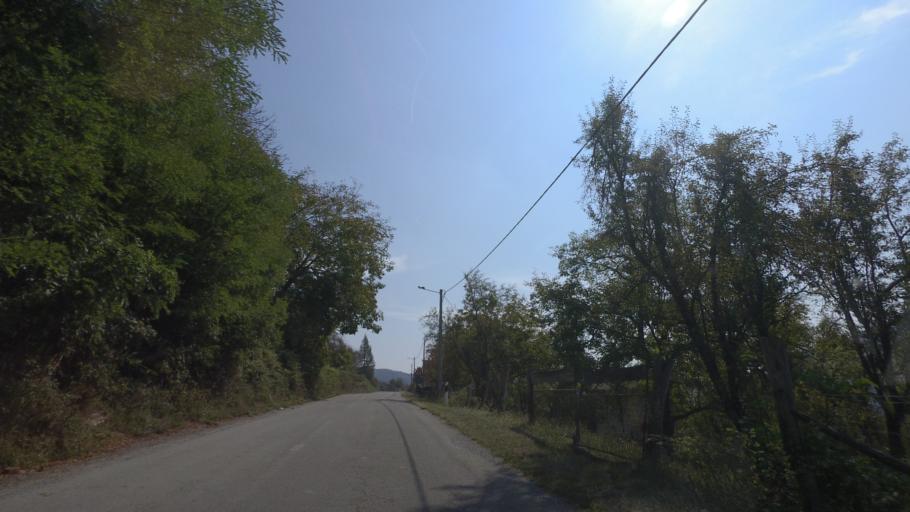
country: BA
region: Federation of Bosnia and Herzegovina
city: Zboriste
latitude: 45.1514
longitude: 16.1450
